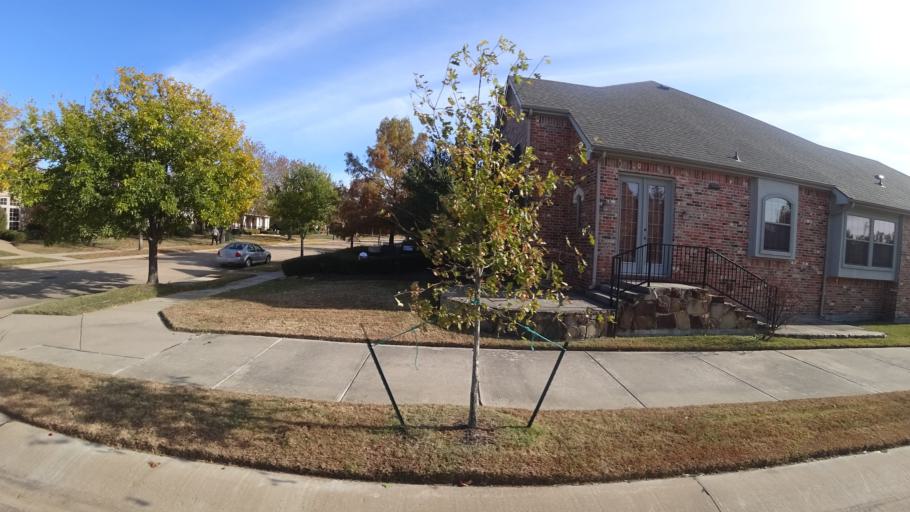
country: US
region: Texas
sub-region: Denton County
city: The Colony
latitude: 33.0327
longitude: -96.9006
